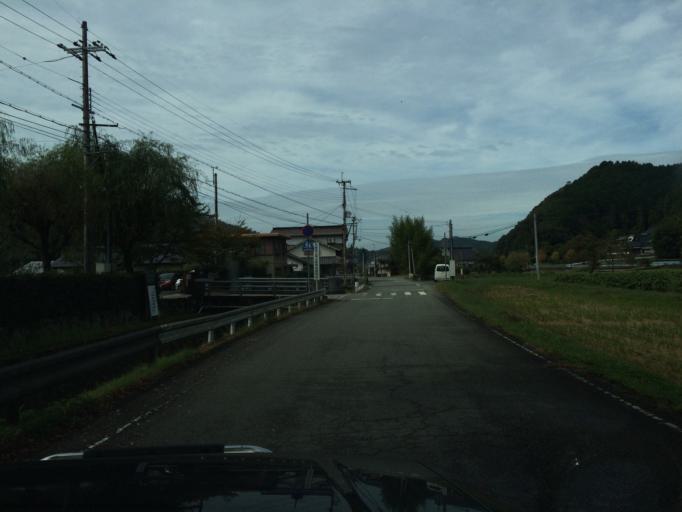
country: JP
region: Hyogo
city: Sasayama
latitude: 35.0717
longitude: 135.3502
